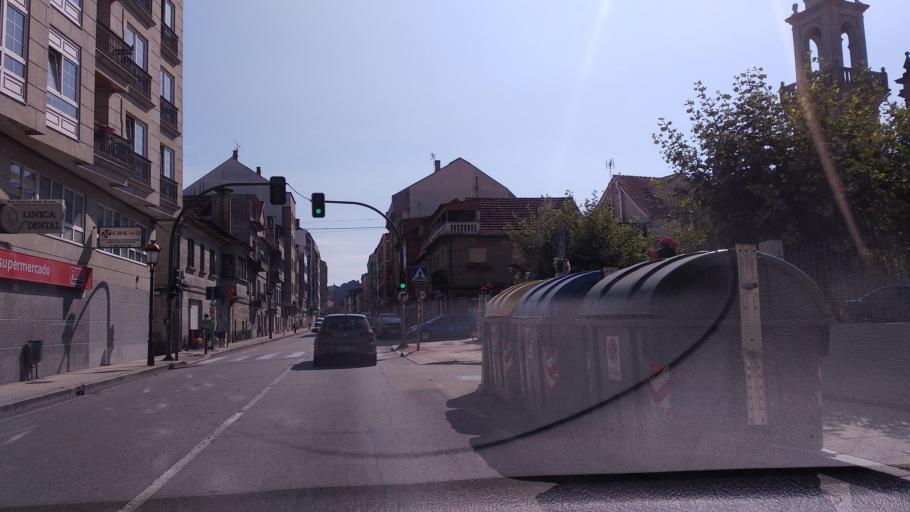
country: ES
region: Galicia
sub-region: Provincia de Pontevedra
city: Moana
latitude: 42.2856
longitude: -8.7343
